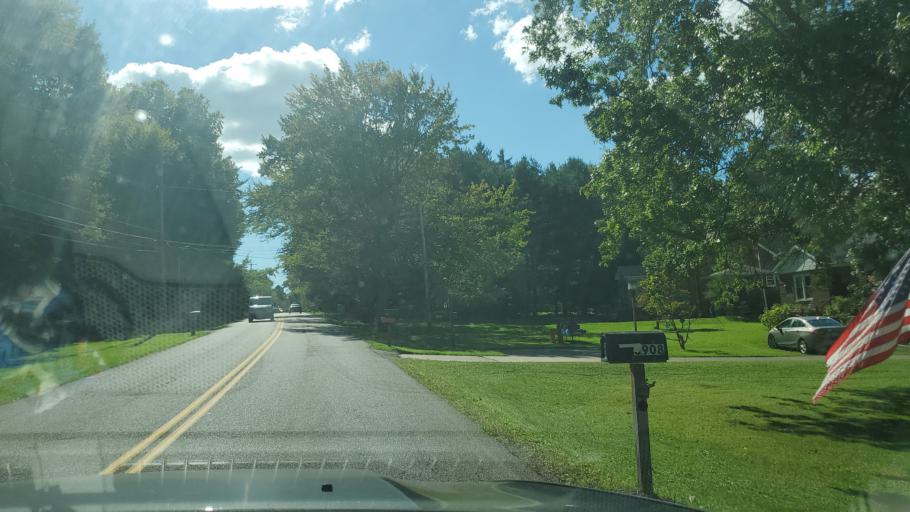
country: US
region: Ohio
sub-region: Mahoning County
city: Canfield
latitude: 41.0457
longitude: -80.7192
